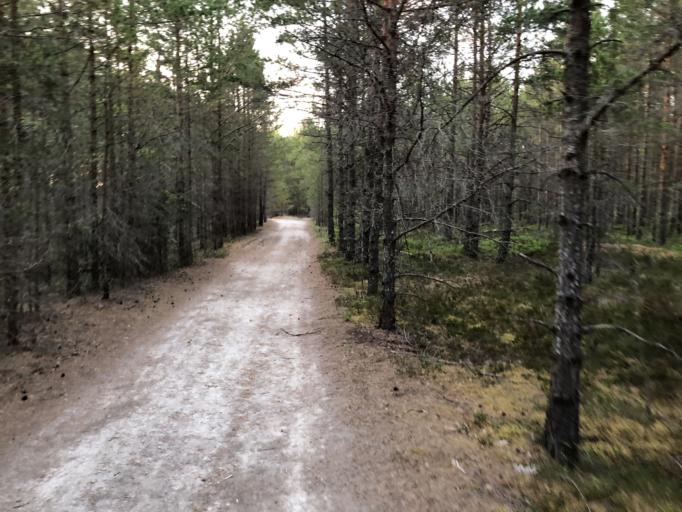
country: EE
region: Harju
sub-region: Paldiski linn
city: Paldiski
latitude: 59.3908
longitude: 24.2329
